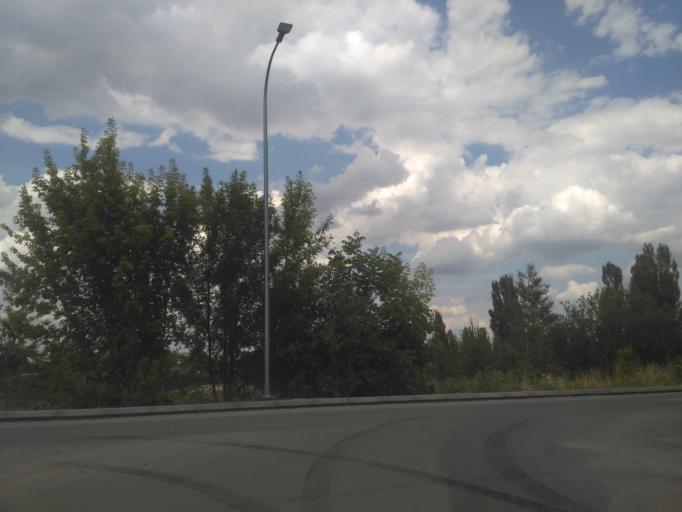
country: PL
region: Lublin Voivodeship
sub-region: Powiat lubelski
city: Jakubowice Murowane
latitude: 51.2361
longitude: 22.6194
